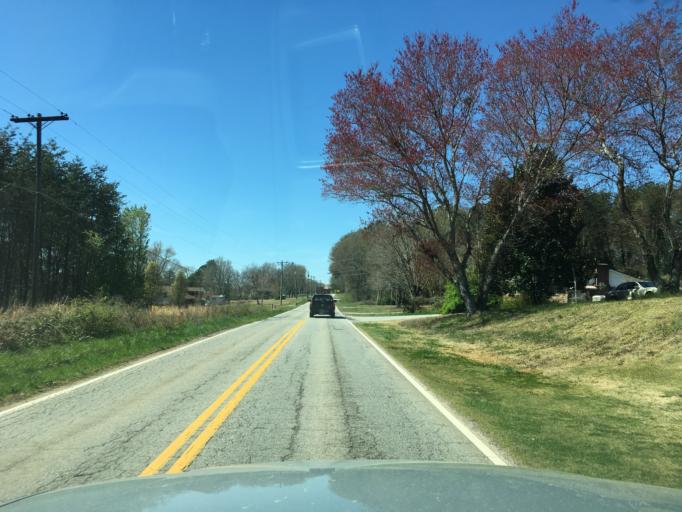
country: US
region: South Carolina
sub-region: Spartanburg County
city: Roebuck
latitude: 34.8884
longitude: -81.9745
